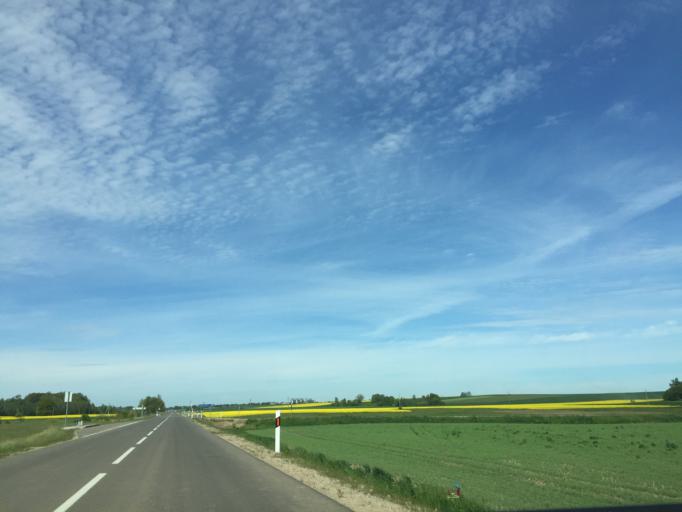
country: LT
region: Panevezys
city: Pasvalys
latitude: 56.1134
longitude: 24.2171
